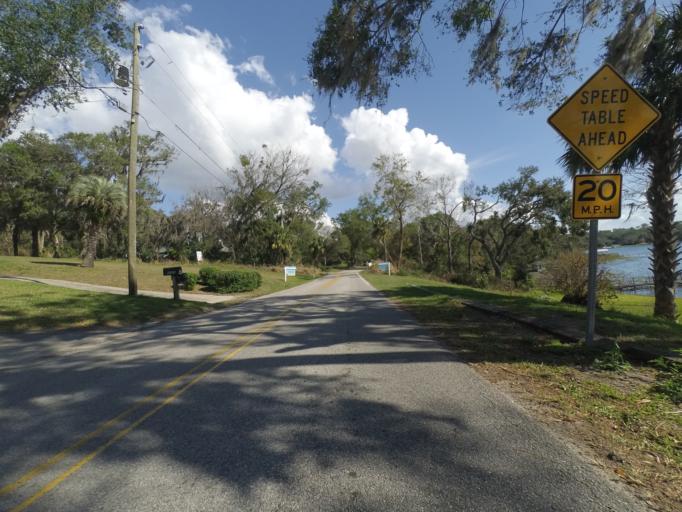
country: US
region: Florida
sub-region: Lake County
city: Mount Dora
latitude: 28.8218
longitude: -81.6546
